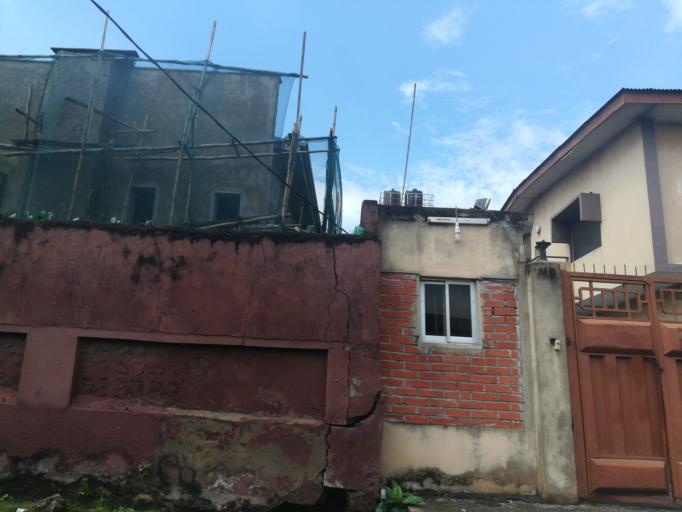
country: NG
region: Lagos
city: Somolu
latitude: 6.5616
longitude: 3.3685
